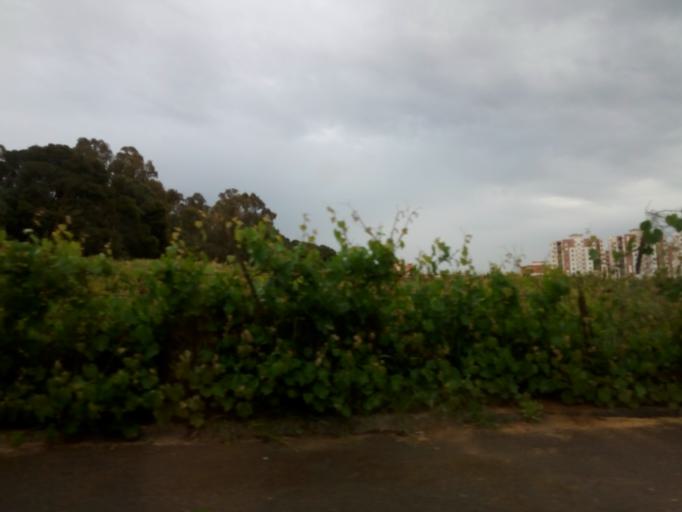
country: DZ
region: Tipaza
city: Saoula
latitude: 36.7311
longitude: 2.9927
